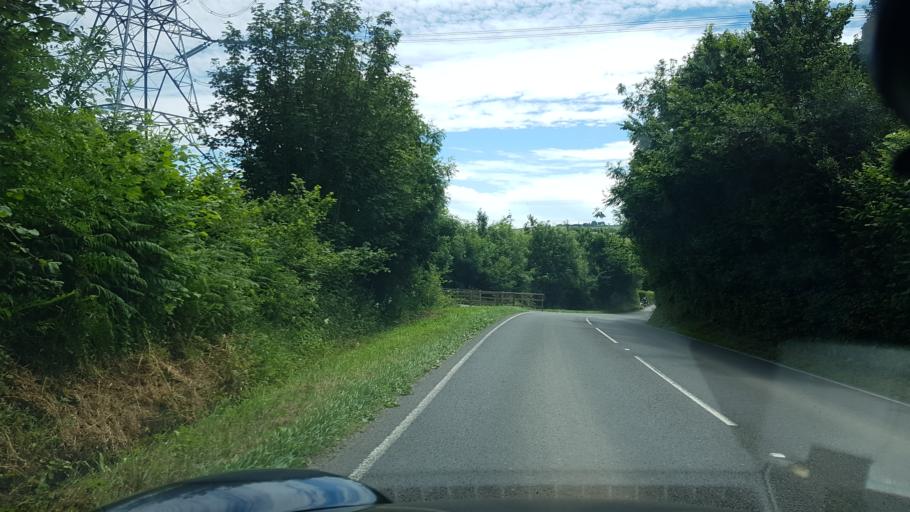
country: GB
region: Wales
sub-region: Carmarthenshire
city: Saint Clears
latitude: 51.7980
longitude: -4.4880
